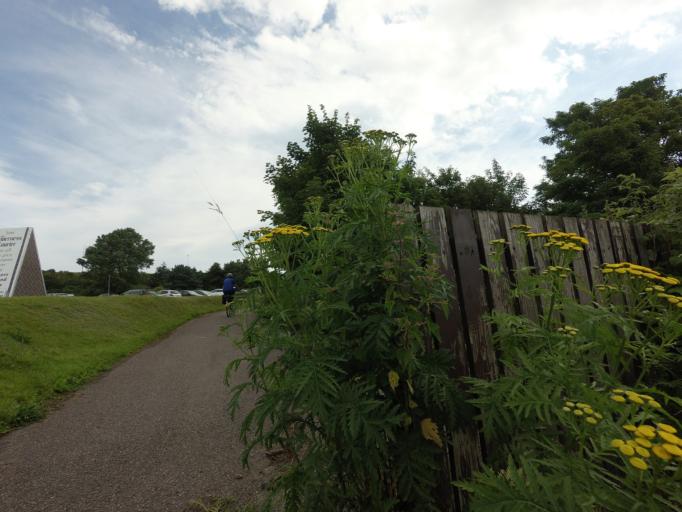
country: GB
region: Scotland
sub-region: Highland
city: Inverness
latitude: 57.4946
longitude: -4.2232
